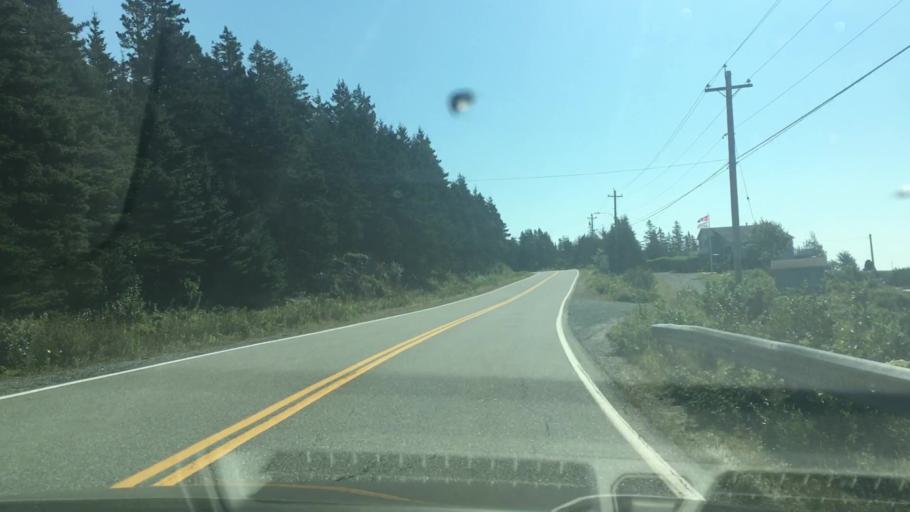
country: CA
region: Nova Scotia
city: Cole Harbour
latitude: 44.8047
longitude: -62.7056
